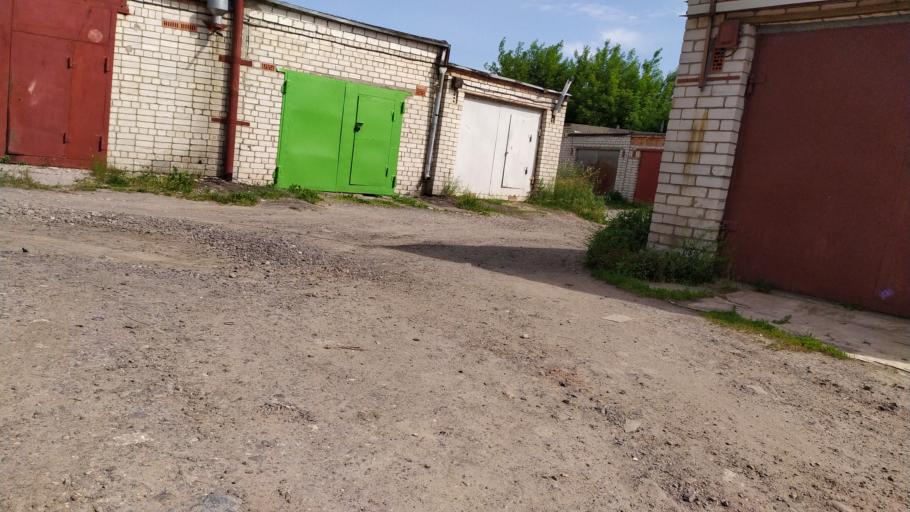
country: RU
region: Kursk
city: Kursk
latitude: 51.6634
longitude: 36.1521
